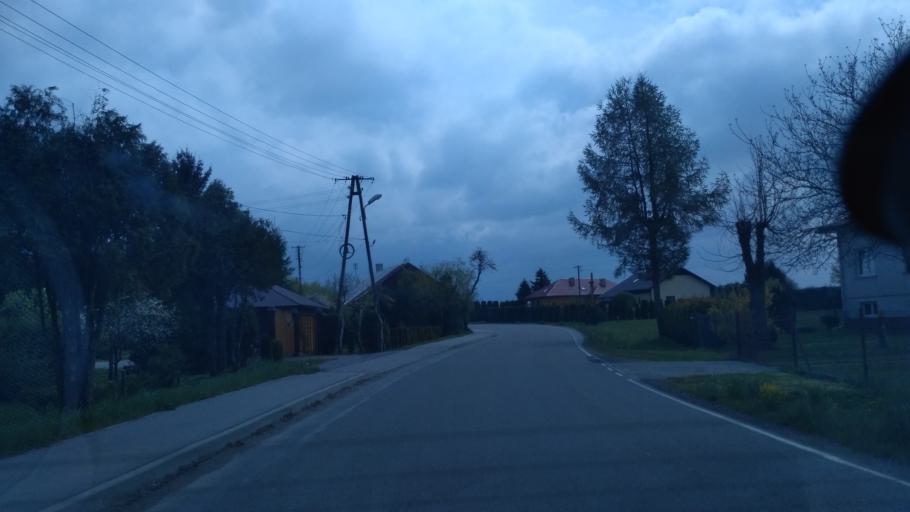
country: PL
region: Subcarpathian Voivodeship
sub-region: Powiat brzozowski
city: Haczow
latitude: 49.6462
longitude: 21.9191
